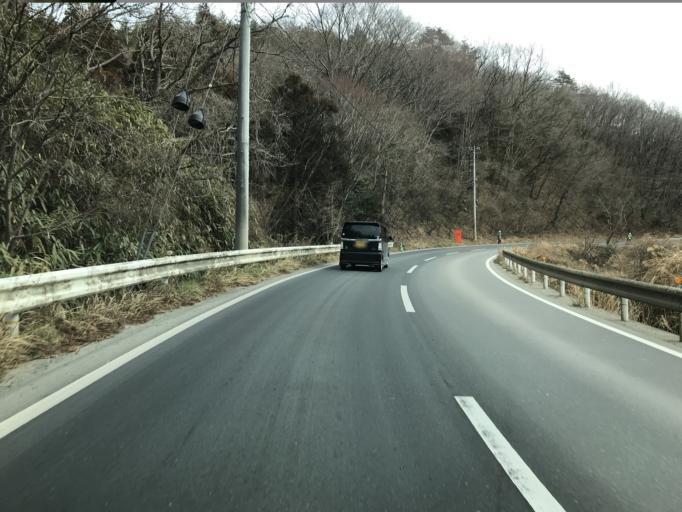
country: JP
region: Fukushima
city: Iwaki
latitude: 37.1106
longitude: 140.8846
